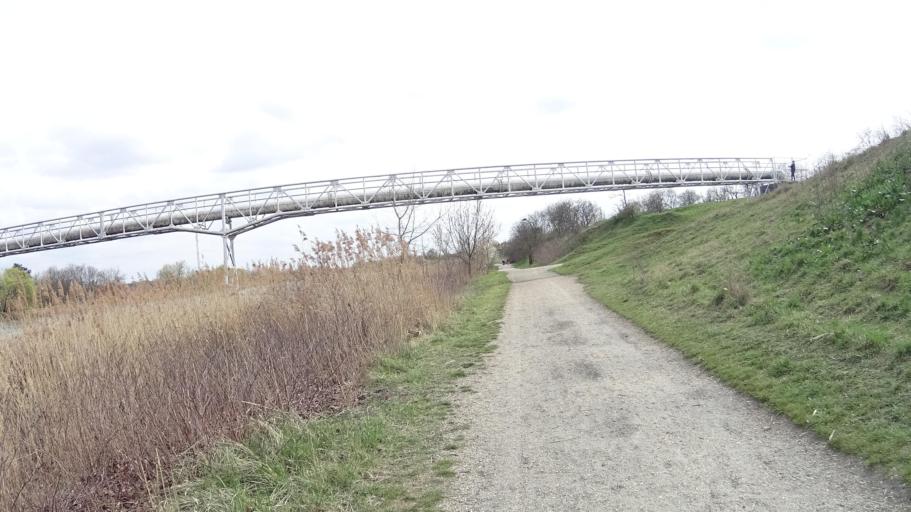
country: HU
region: Budapest
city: Budapest XX. keruelet
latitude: 47.4234
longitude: 19.0920
